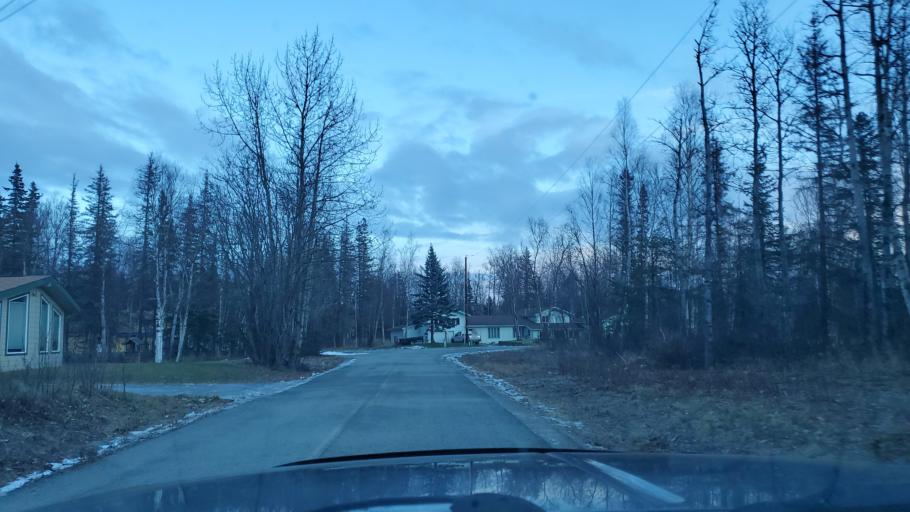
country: US
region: Alaska
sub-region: Matanuska-Susitna Borough
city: Wasilla
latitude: 61.5916
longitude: -149.4119
